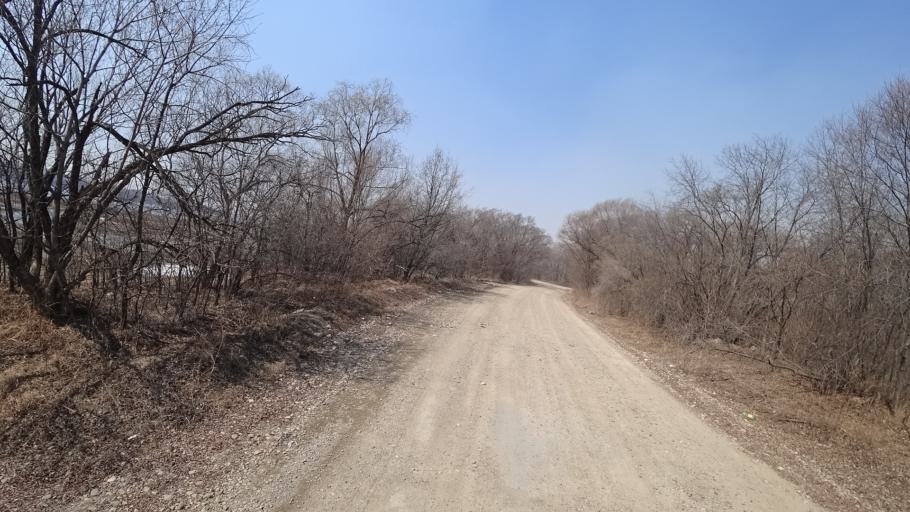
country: RU
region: Amur
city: Novobureyskiy
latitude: 49.7888
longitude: 129.9086
